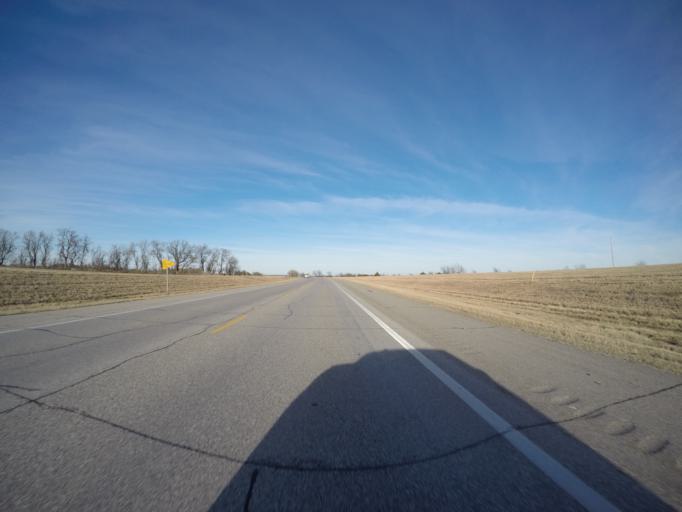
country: US
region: Kansas
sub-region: Harvey County
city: North Newton
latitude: 38.1375
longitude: -97.2337
